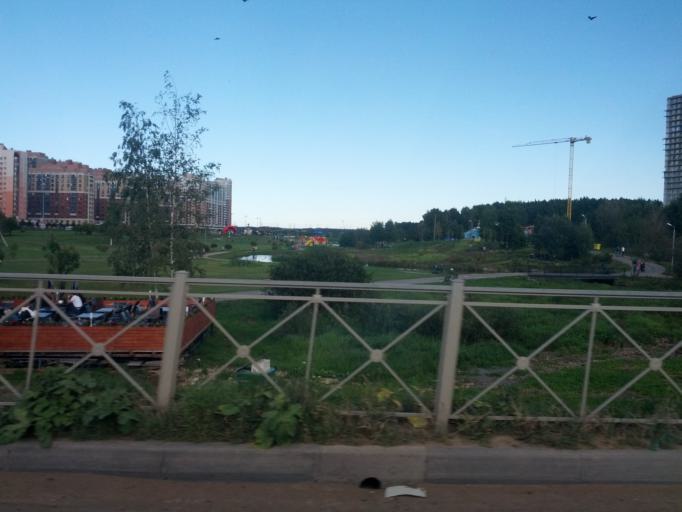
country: RU
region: St.-Petersburg
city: Krasnogvargeisky
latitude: 59.9112
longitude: 30.5072
